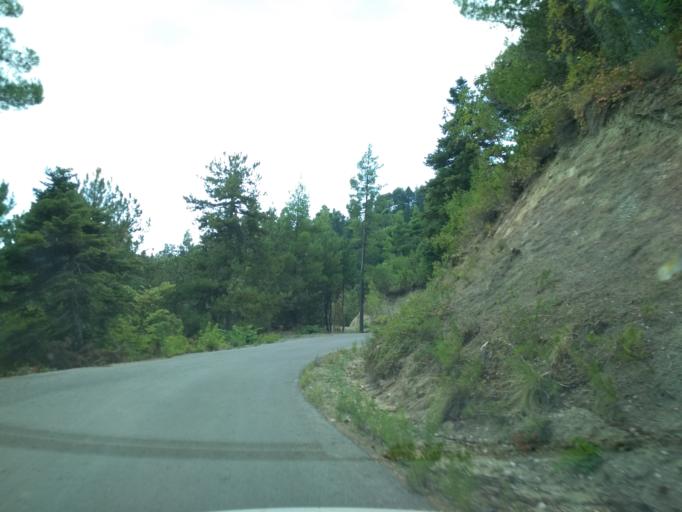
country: GR
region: Central Greece
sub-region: Nomos Evvoias
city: Roviai
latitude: 38.8600
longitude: 23.2855
